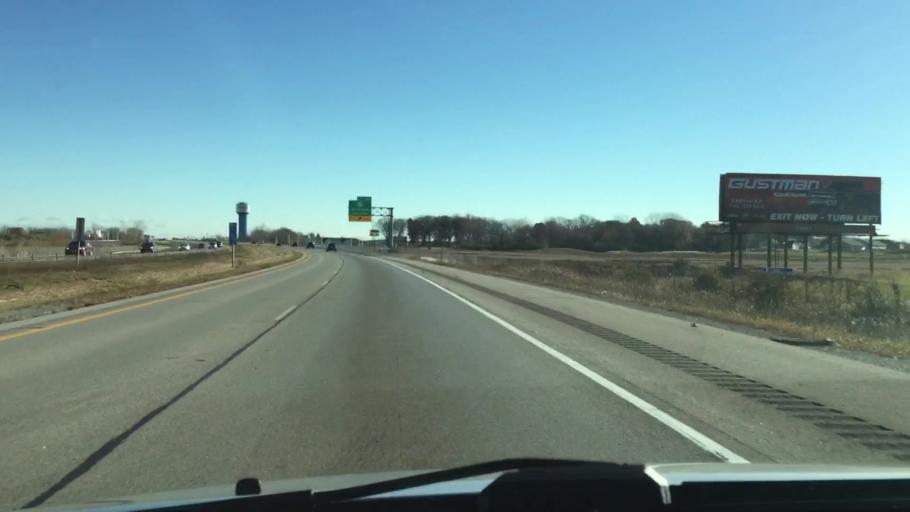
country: US
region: Wisconsin
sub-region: Outagamie County
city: Kaukauna
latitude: 44.2976
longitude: -88.2805
